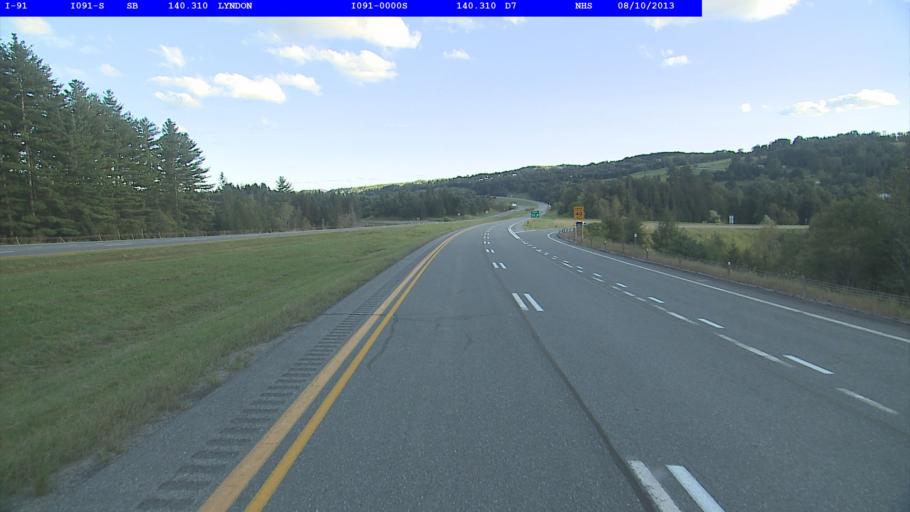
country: US
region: Vermont
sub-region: Caledonia County
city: Lyndonville
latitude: 44.5590
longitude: -72.0287
